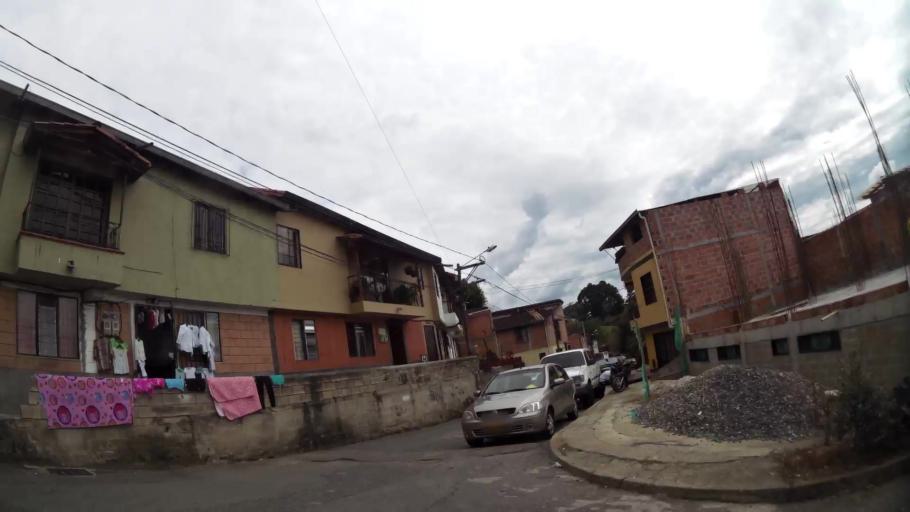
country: CO
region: Antioquia
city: Rionegro
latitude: 6.1534
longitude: -75.3658
